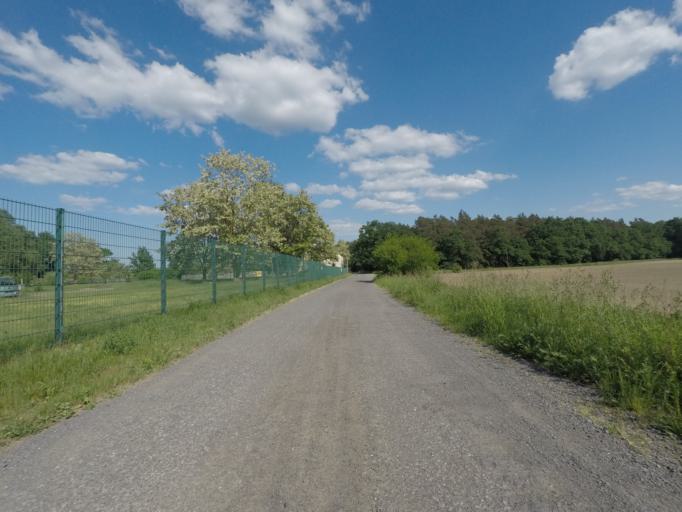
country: DE
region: Brandenburg
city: Britz
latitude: 52.8688
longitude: 13.7747
